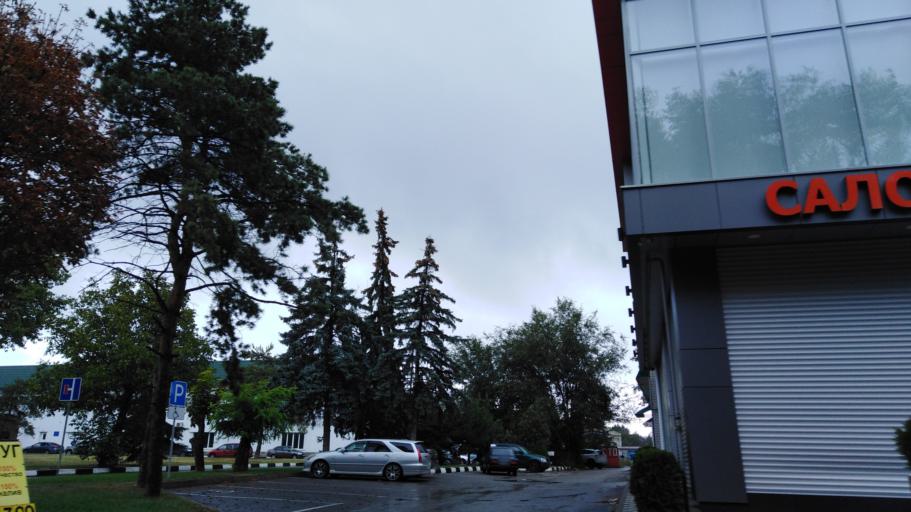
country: RU
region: Stavropol'skiy
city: Yessentukskaya
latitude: 44.0544
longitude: 42.9052
